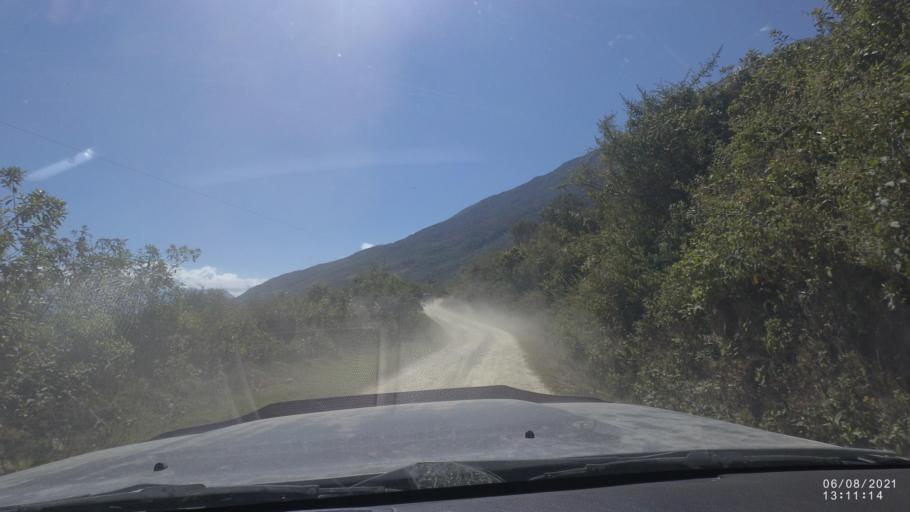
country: BO
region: La Paz
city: Quime
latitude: -16.7209
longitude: -66.7062
